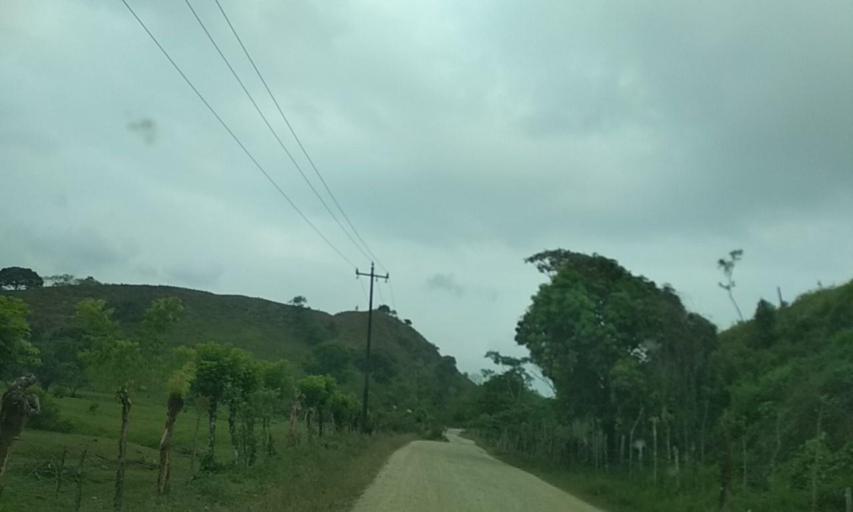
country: MX
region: Veracruz
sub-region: Uxpanapa
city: Poblado 10
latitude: 17.4560
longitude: -94.0950
